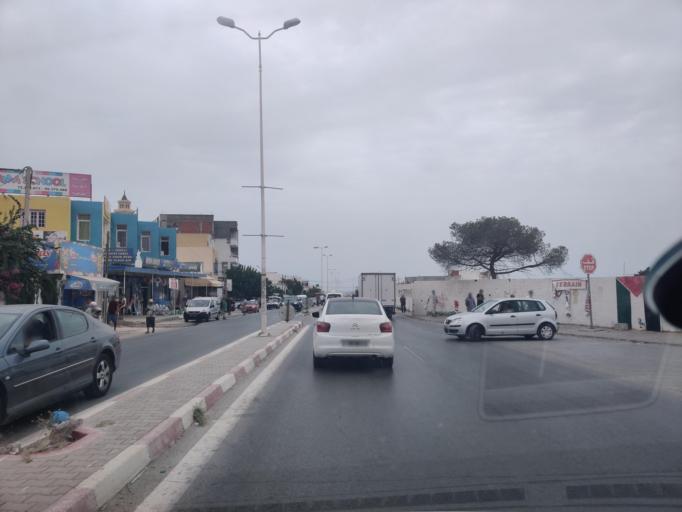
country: TN
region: Nabul
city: Al Hammamat
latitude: 36.4082
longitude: 10.6309
